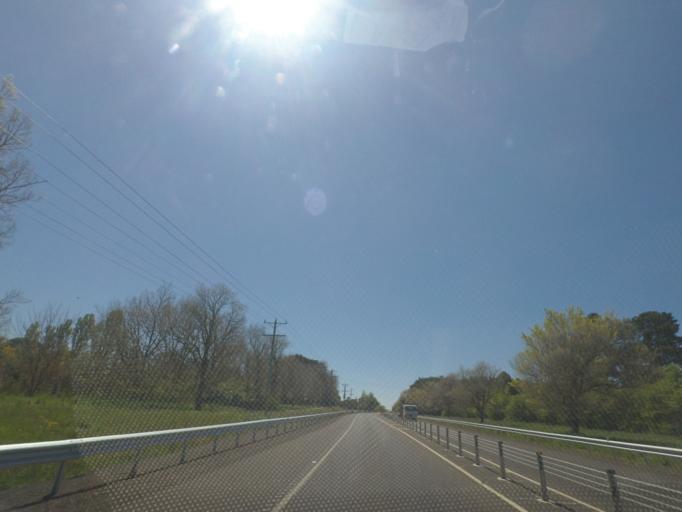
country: AU
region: Victoria
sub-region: Hume
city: Sunbury
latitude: -37.3342
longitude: 144.7410
